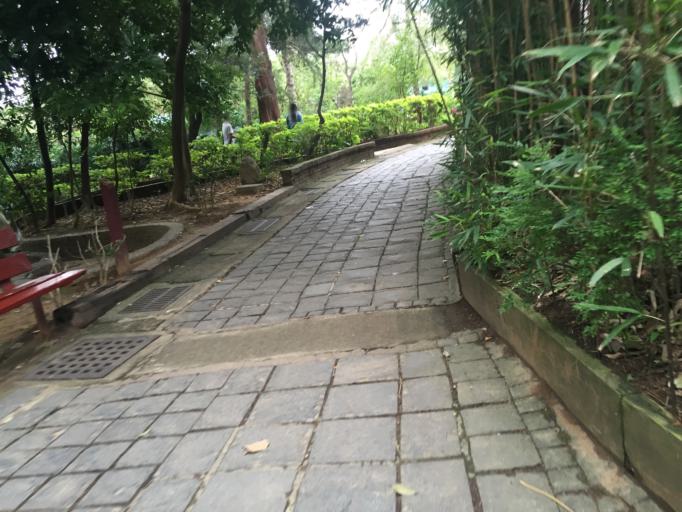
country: TW
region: Taiwan
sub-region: Hsinchu
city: Hsinchu
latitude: 24.8013
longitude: 120.9794
